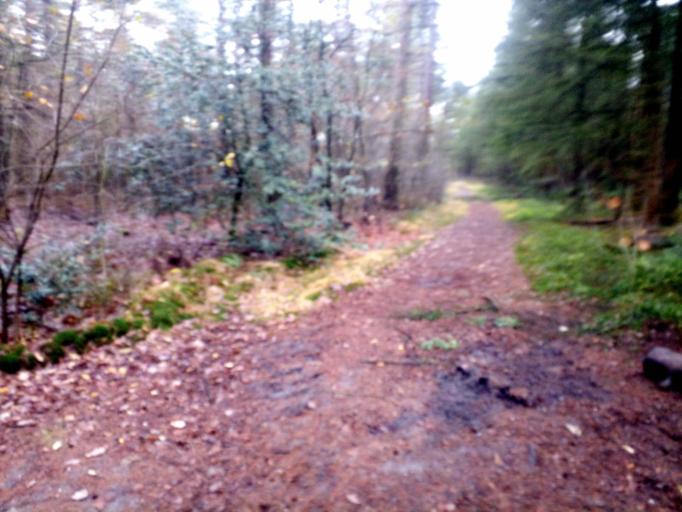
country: NL
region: Utrecht
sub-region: Gemeente Utrechtse Heuvelrug
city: Maarn
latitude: 52.0956
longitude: 5.3277
